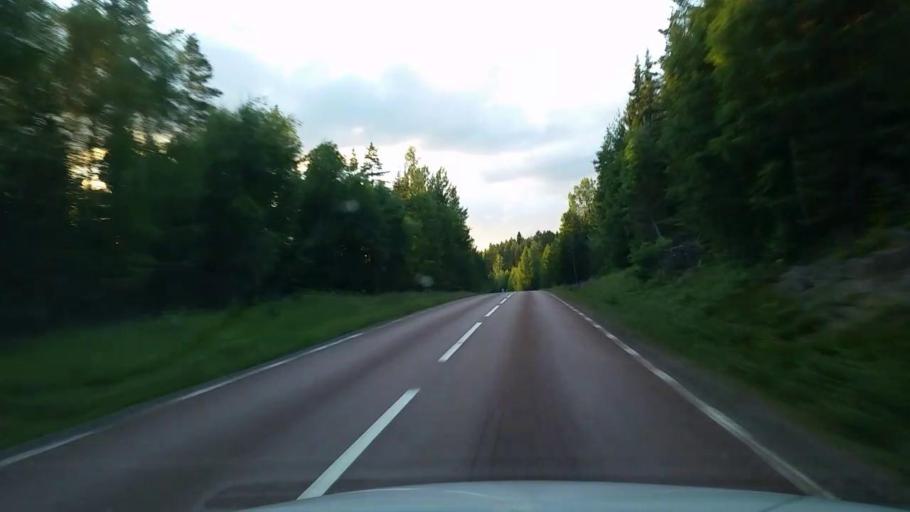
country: SE
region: Vaesternorrland
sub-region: Ange Kommun
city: Ange
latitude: 62.1498
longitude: 15.6829
